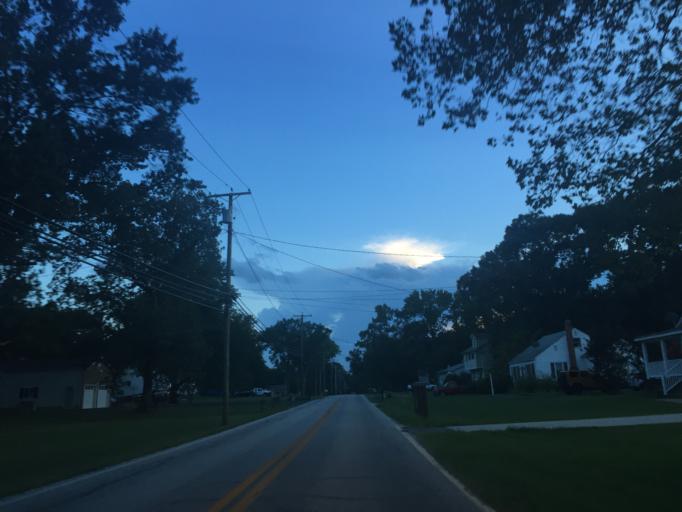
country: US
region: Maryland
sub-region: Baltimore County
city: Bowleys Quarters
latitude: 39.3674
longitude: -76.3626
